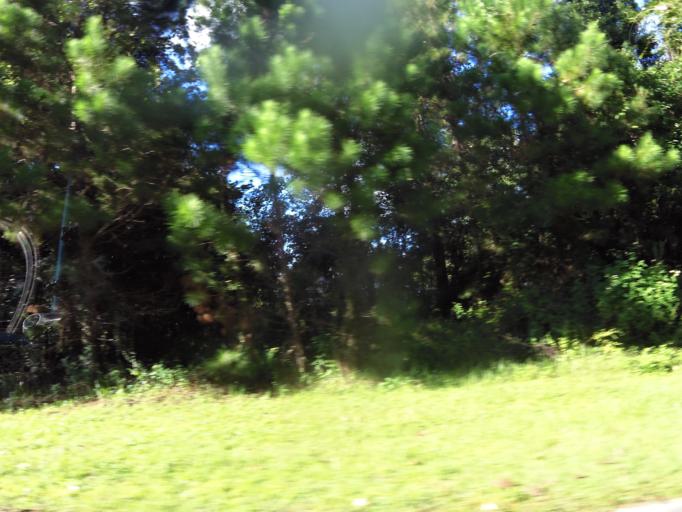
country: US
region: Florida
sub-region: Wakulla County
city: Crawfordville
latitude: 30.0624
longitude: -84.4923
